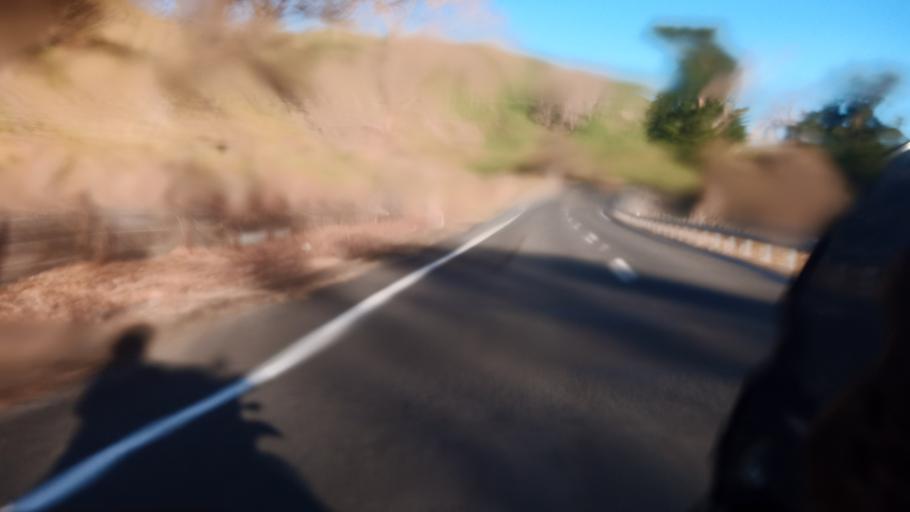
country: NZ
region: Hawke's Bay
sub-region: Wairoa District
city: Wairoa
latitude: -39.0160
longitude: 177.3541
